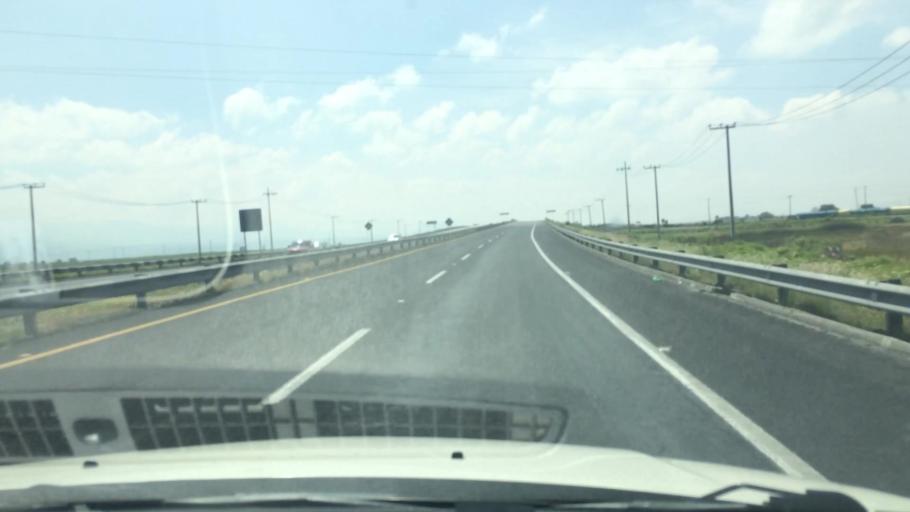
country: MX
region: Mexico
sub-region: Toluca
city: La Constitucion Toltepec
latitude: 19.3645
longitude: -99.5385
